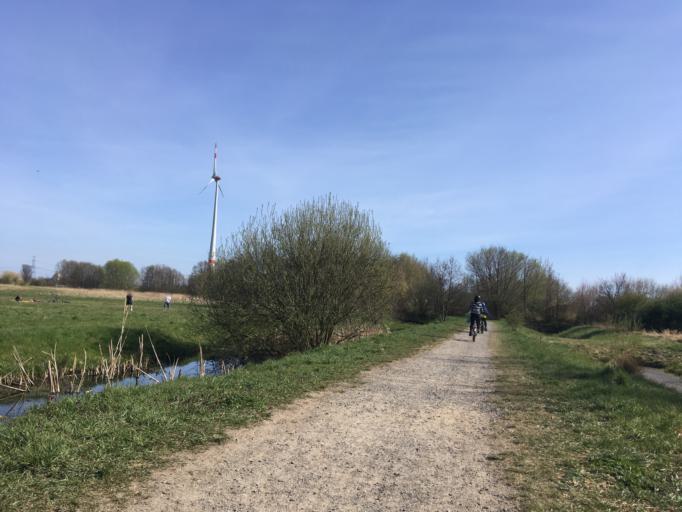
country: DE
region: Berlin
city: Karow
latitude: 52.5999
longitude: 13.4926
